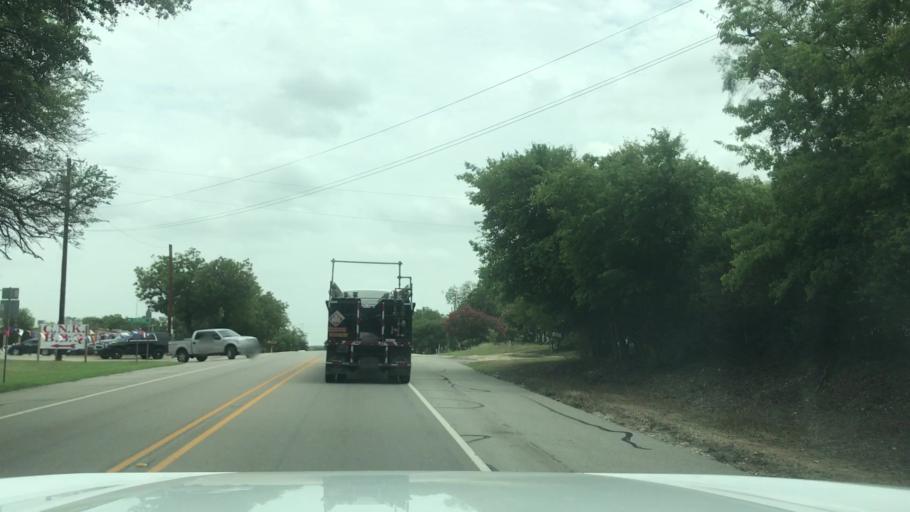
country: US
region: Texas
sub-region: Bosque County
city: Valley Mills
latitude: 31.6608
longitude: -97.4785
